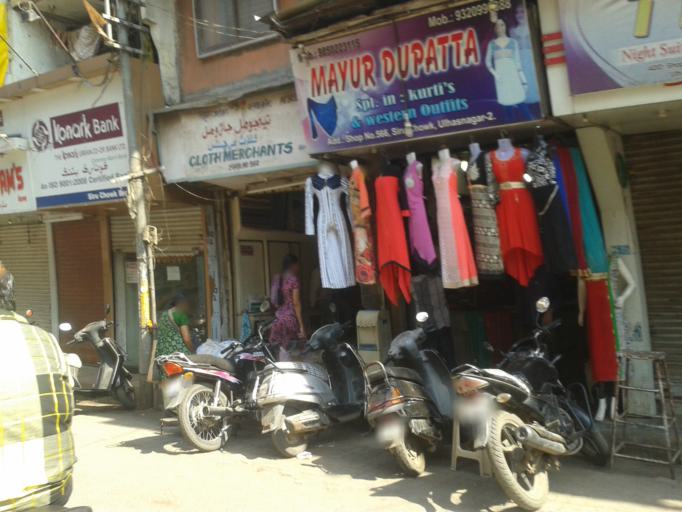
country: IN
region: Maharashtra
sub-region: Thane
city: Ulhasnagar
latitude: 19.2354
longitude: 73.1650
